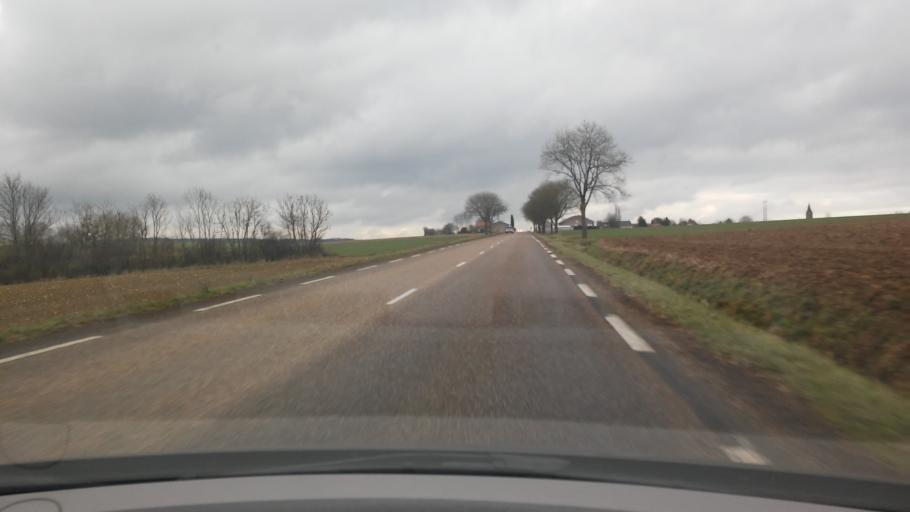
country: FR
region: Lorraine
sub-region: Departement de la Moselle
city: Retonfey
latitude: 49.1155
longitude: 6.2952
